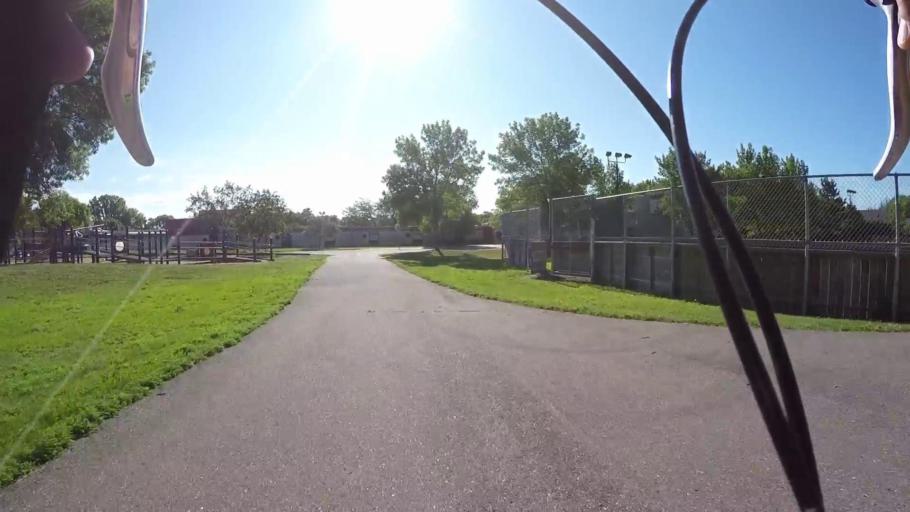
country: US
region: Minnesota
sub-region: Carver County
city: Chanhassen
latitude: 44.8768
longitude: -93.5002
